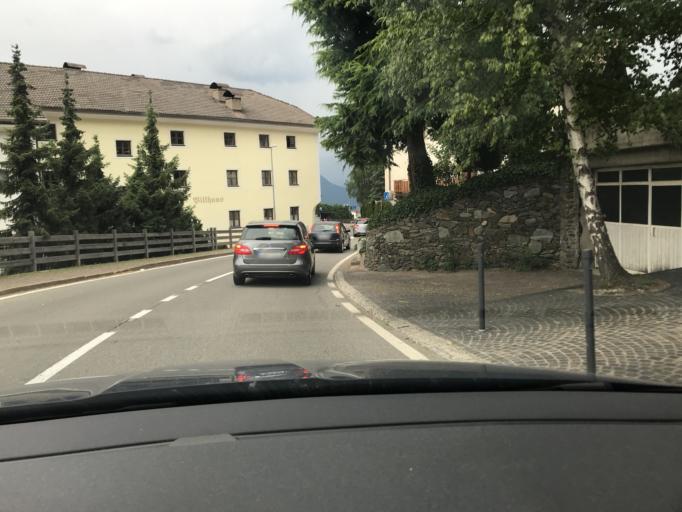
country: IT
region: Trentino-Alto Adige
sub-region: Bolzano
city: Bressanone
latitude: 46.6984
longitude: 11.6761
